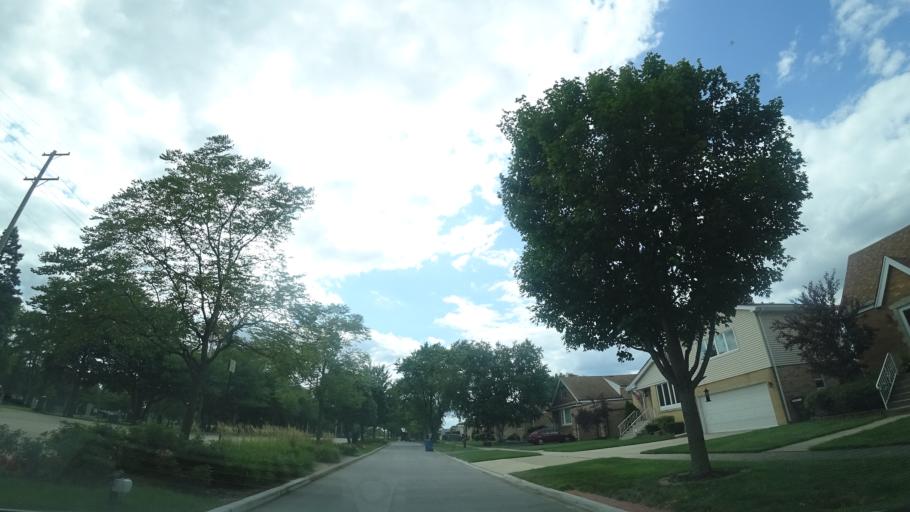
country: US
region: Illinois
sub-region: Cook County
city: Alsip
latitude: 41.6913
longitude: -87.7266
